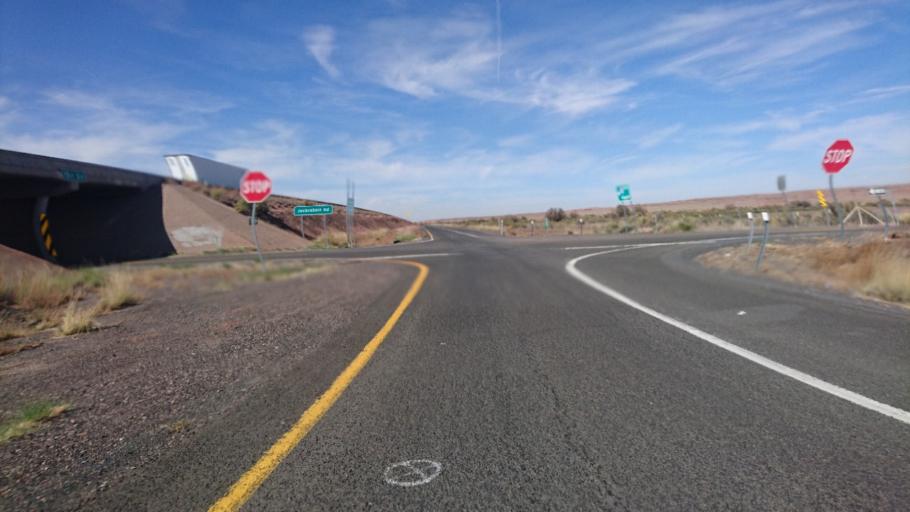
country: US
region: Arizona
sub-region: Navajo County
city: Joseph City
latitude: 34.9696
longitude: -110.4332
